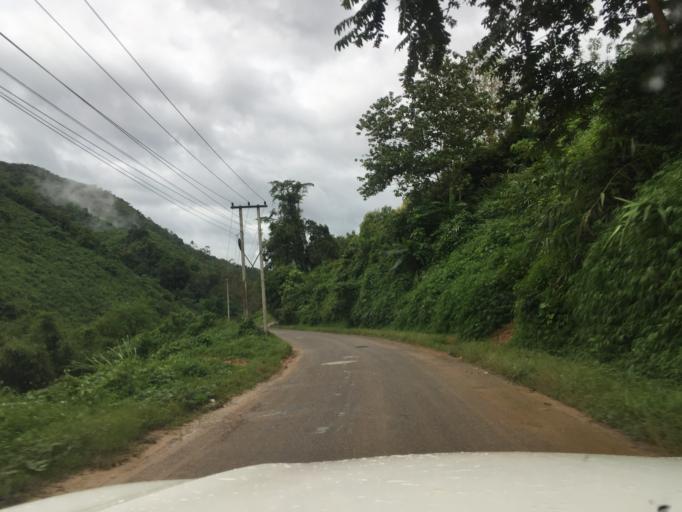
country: LA
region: Oudomxai
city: Muang La
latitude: 20.9941
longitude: 102.2302
